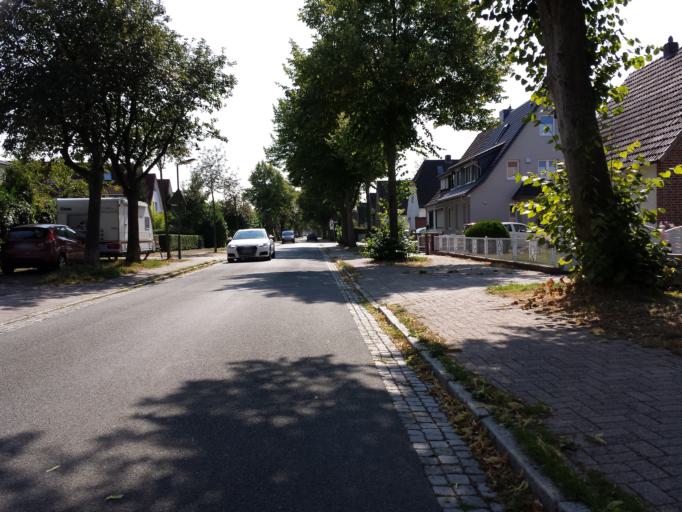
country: DE
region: Bremen
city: Bremen
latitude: 53.0424
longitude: 8.8571
